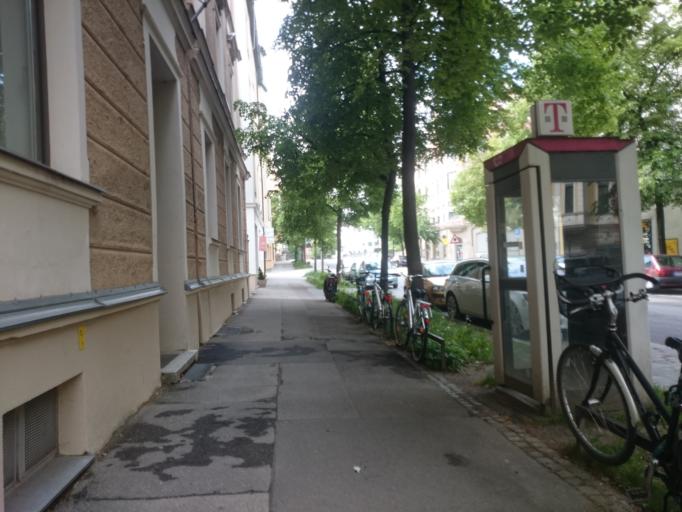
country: DE
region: Bavaria
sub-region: Swabia
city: Augsburg
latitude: 48.3579
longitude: 10.8974
